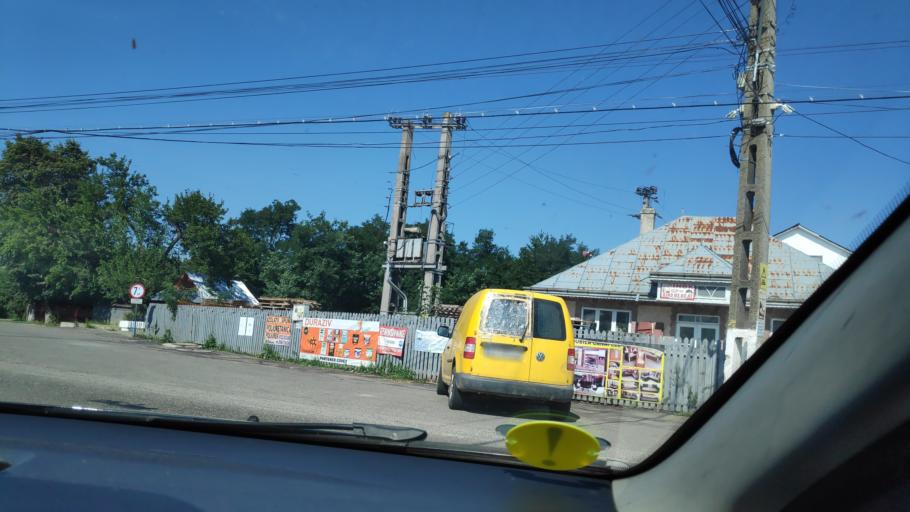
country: RO
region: Suceava
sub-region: Comuna Boroaia
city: Boroaia
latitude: 47.3482
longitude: 26.3369
